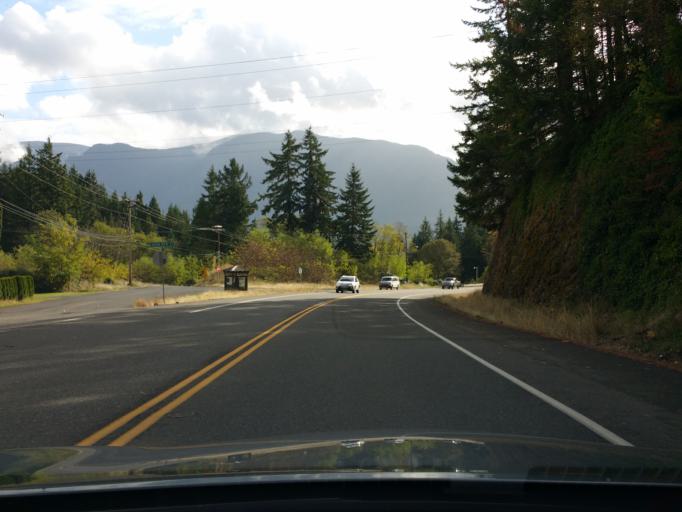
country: US
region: Washington
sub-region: Skamania County
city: Carson
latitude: 45.7234
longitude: -121.8203
